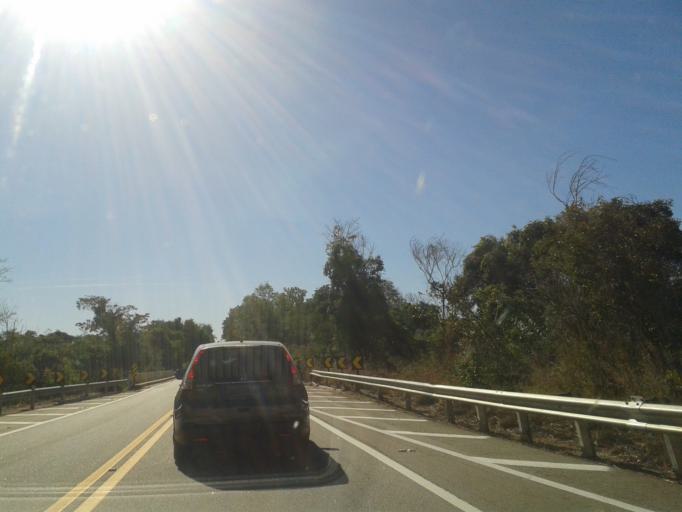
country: BR
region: Goias
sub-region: Itapuranga
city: Itapuranga
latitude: -15.5826
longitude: -50.2685
